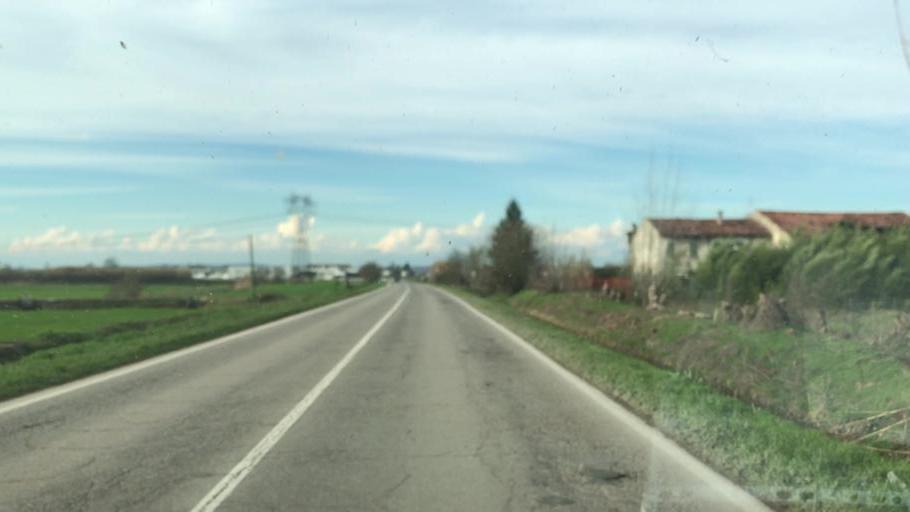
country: IT
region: Lombardy
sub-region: Provincia di Mantova
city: Cerlongo
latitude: 45.2690
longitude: 10.6616
